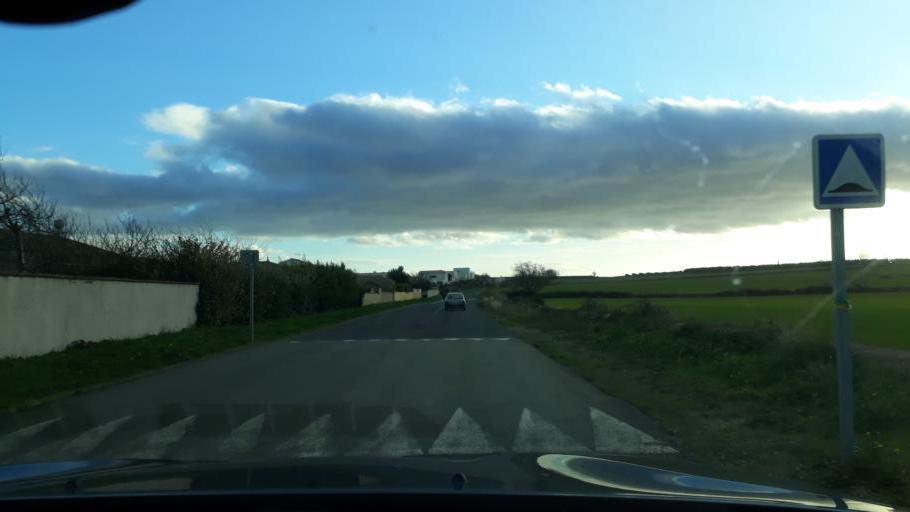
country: FR
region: Languedoc-Roussillon
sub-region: Departement de l'Herault
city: Colombiers
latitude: 43.3110
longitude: 3.1395
